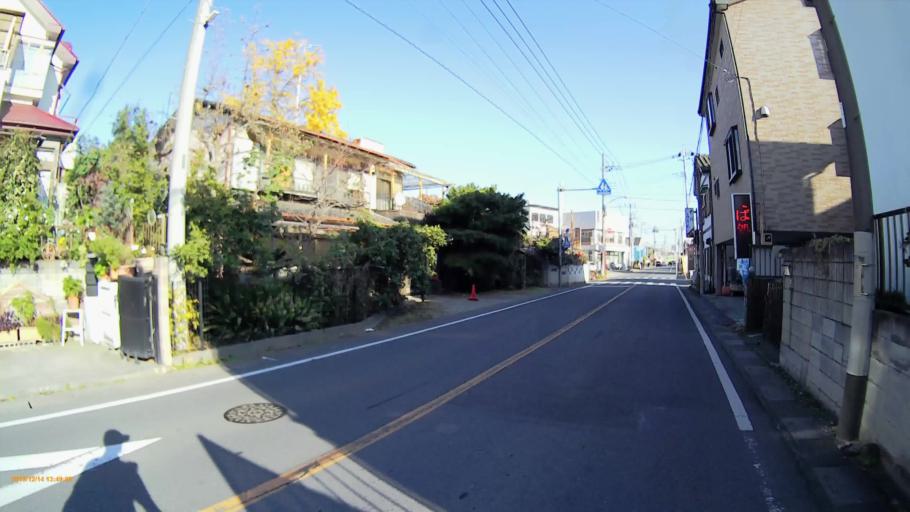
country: JP
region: Saitama
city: Konosu
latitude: 36.0680
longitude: 139.5013
